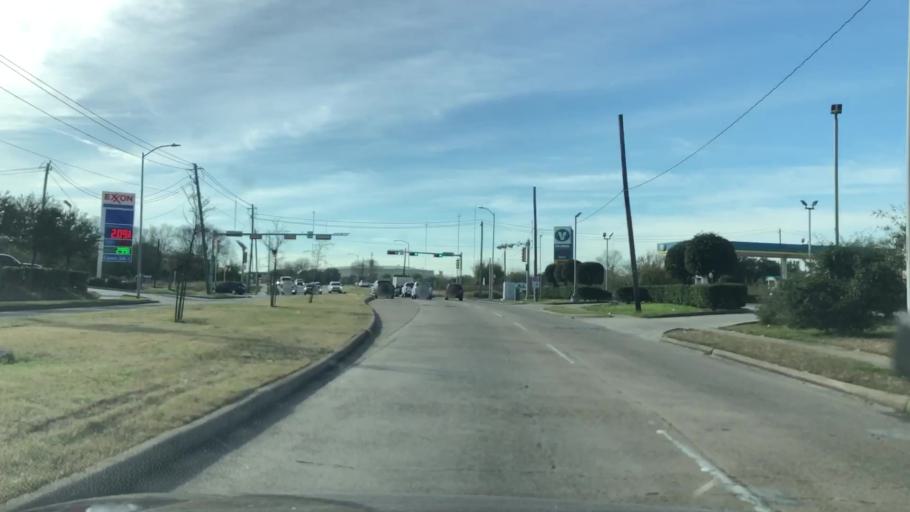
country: US
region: Texas
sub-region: Fort Bend County
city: Missouri City
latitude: 29.6278
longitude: -95.4951
